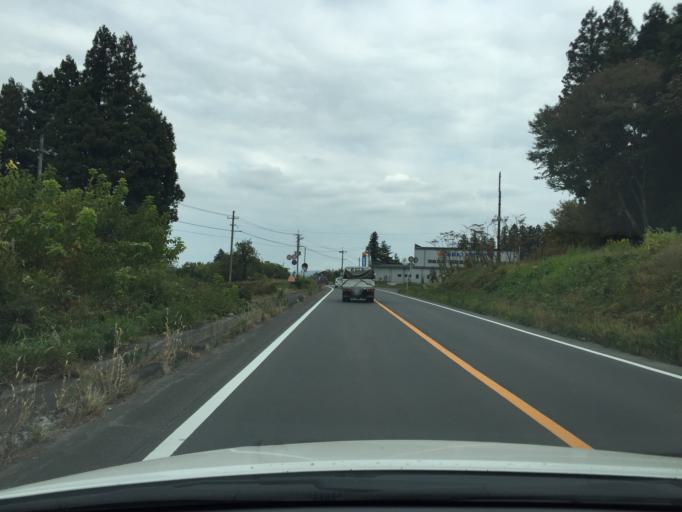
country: JP
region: Fukushima
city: Ishikawa
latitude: 37.0559
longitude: 140.3278
